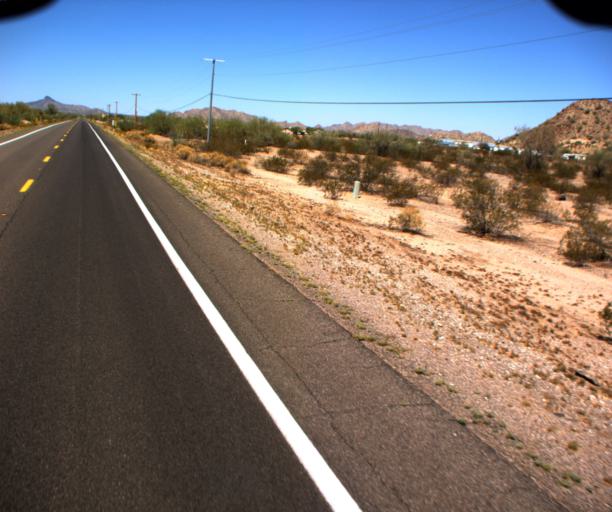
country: US
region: Arizona
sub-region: Pinal County
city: Maricopa
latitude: 32.8672
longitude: -112.0632
